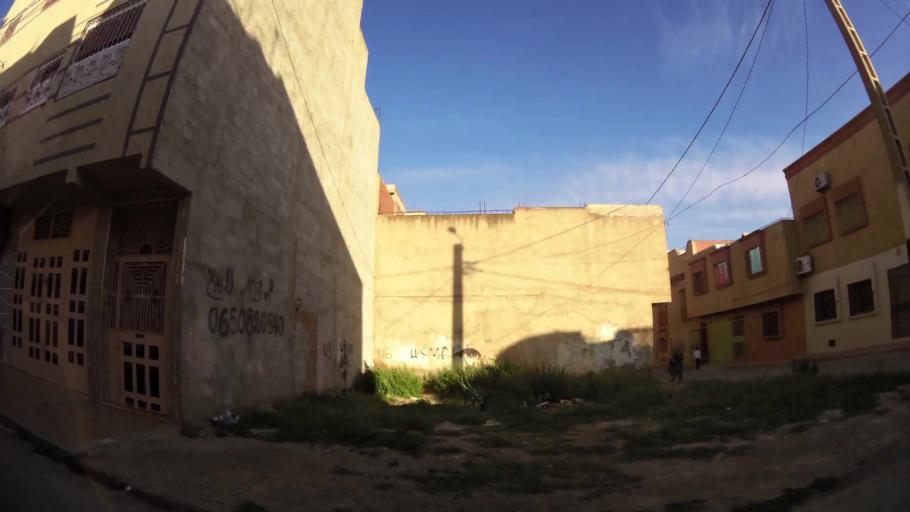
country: MA
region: Oriental
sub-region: Oujda-Angad
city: Oujda
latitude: 34.7077
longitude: -1.8938
